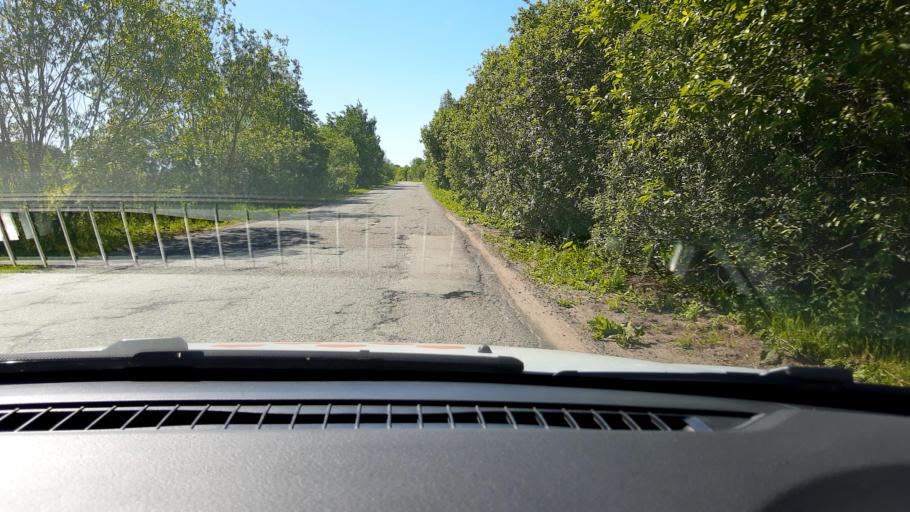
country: RU
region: Nizjnij Novgorod
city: Bor
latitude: 56.3951
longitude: 44.0982
